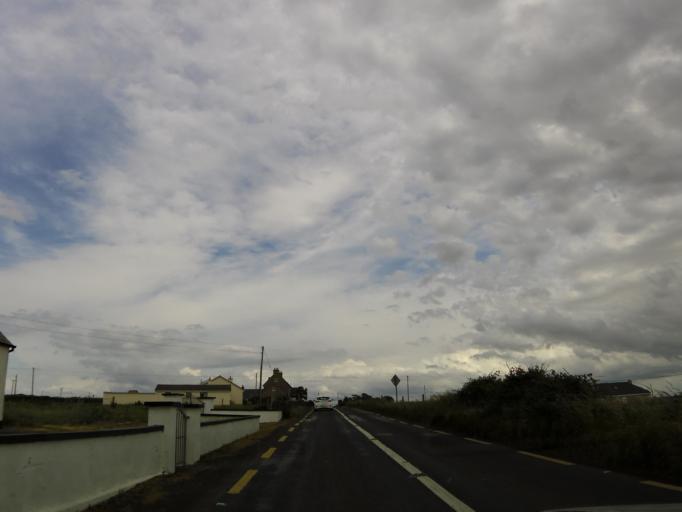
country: IE
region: Munster
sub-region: An Clar
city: Kilrush
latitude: 52.7219
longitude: -9.5827
